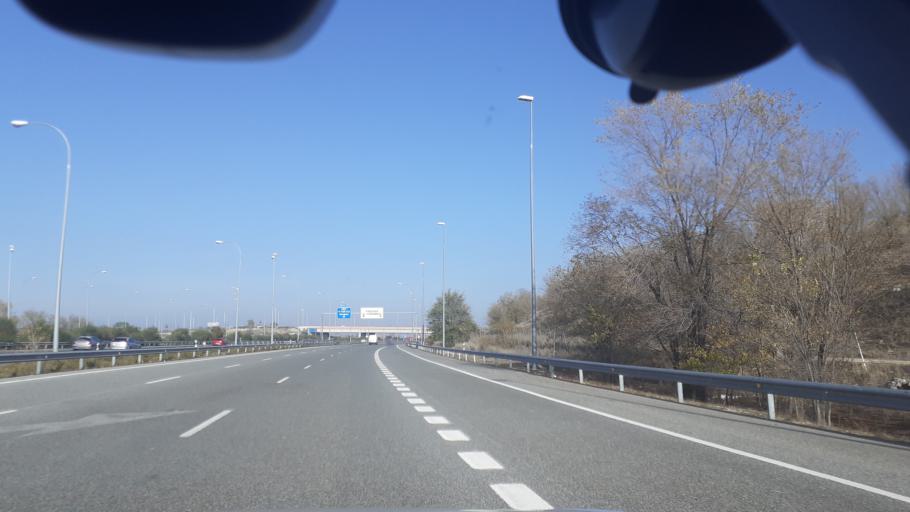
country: ES
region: Madrid
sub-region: Provincia de Madrid
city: Coslada
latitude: 40.4050
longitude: -3.5703
